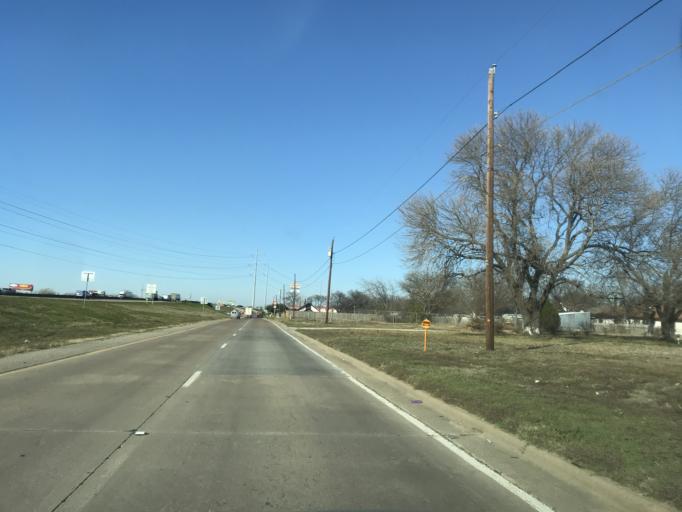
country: US
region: Texas
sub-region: Dallas County
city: Cockrell Hill
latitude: 32.7753
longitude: -96.9157
